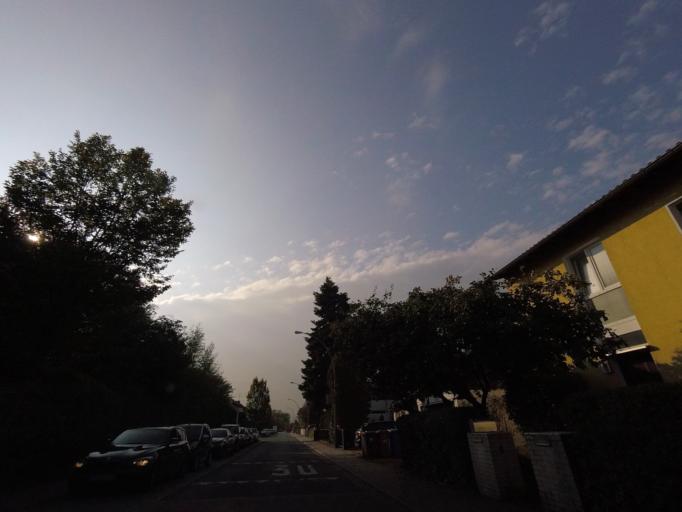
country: DE
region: Hesse
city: Schwalbach am Taunus
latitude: 50.1474
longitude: 8.5400
